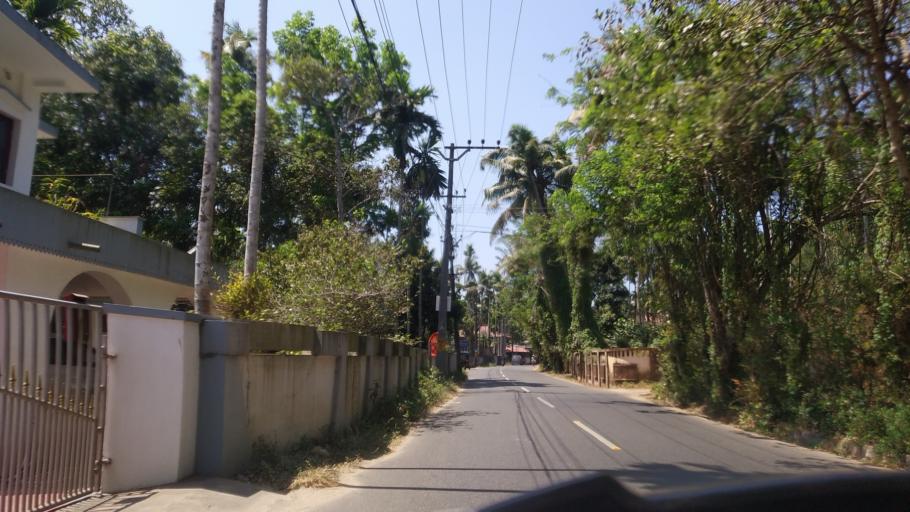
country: IN
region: Kerala
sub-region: Thrissur District
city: Kodungallur
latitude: 10.1780
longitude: 76.2139
